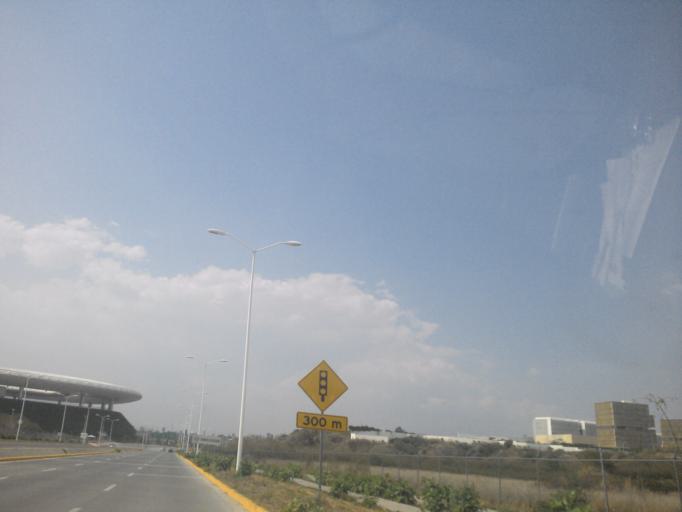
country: MX
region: Jalisco
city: Guadalajara
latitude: 20.6766
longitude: -103.4616
